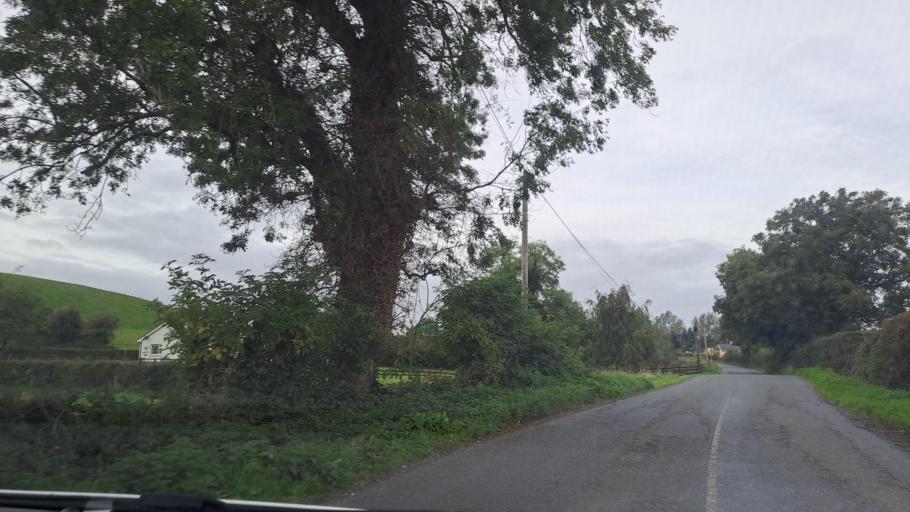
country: IE
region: Ulster
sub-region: County Monaghan
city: Carrickmacross
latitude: 53.8595
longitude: -6.6754
